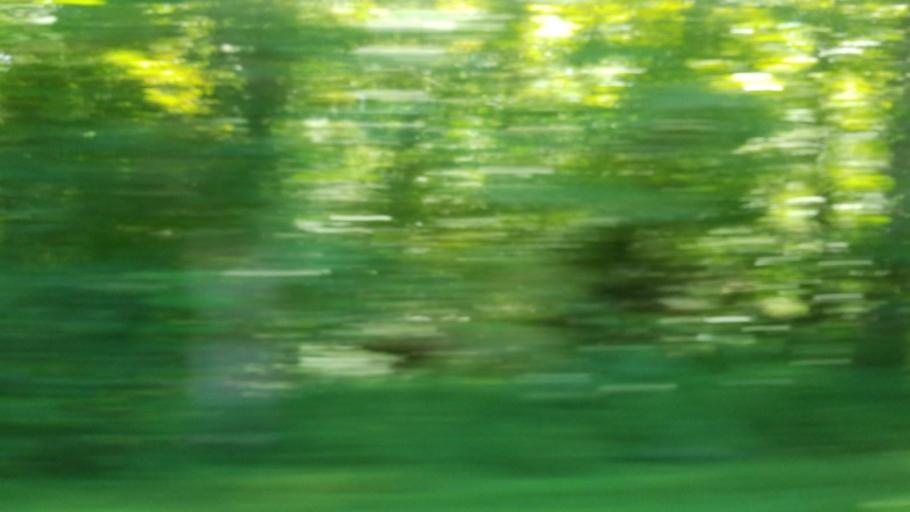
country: US
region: Illinois
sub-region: Williamson County
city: Johnston City
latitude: 37.7894
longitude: -88.8923
